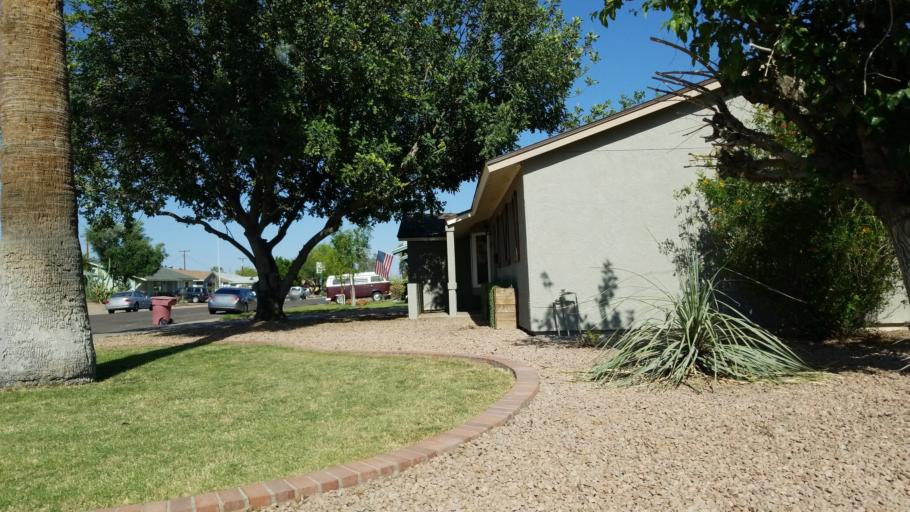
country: US
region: Arizona
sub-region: Maricopa County
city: Scottsdale
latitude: 33.4693
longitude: -111.9004
